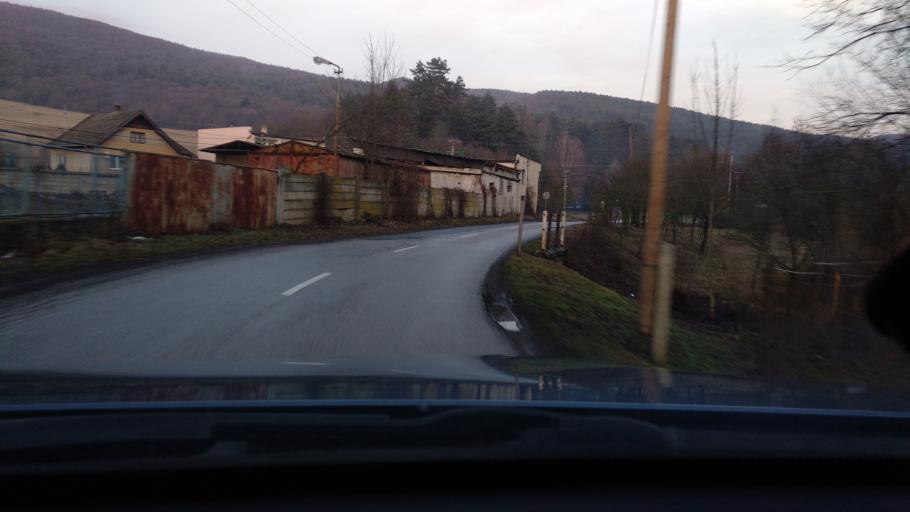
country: SK
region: Nitriansky
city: Trencianske Teplice
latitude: 48.8429
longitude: 18.2435
